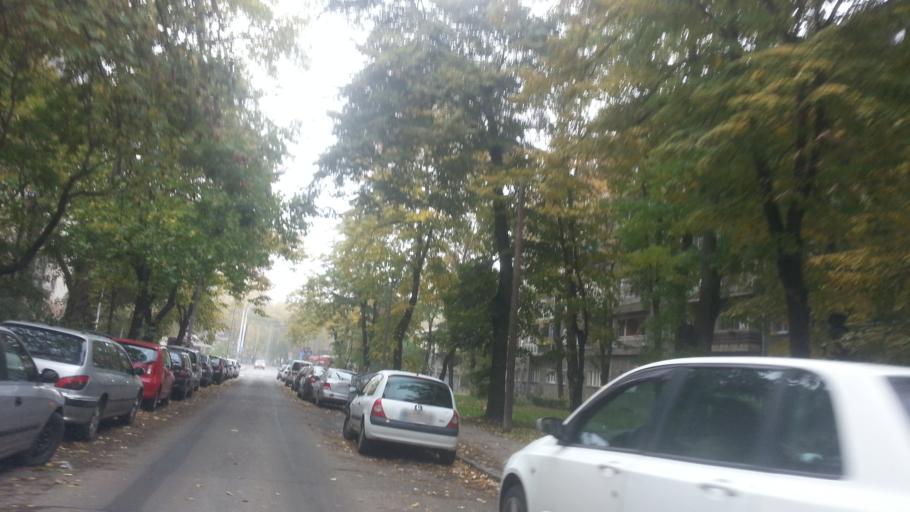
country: RS
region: Central Serbia
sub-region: Belgrade
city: Zemun
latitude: 44.8312
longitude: 20.4041
